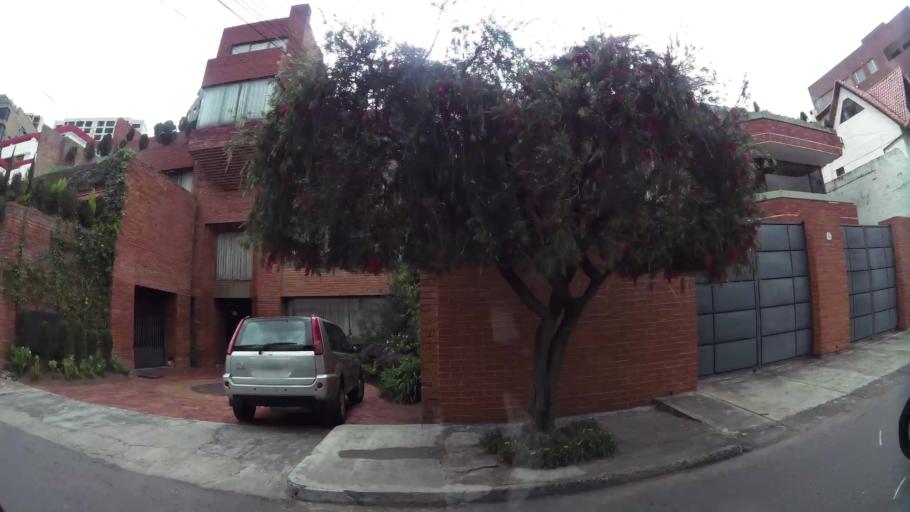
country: EC
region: Pichincha
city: Quito
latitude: -0.1664
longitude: -78.4954
